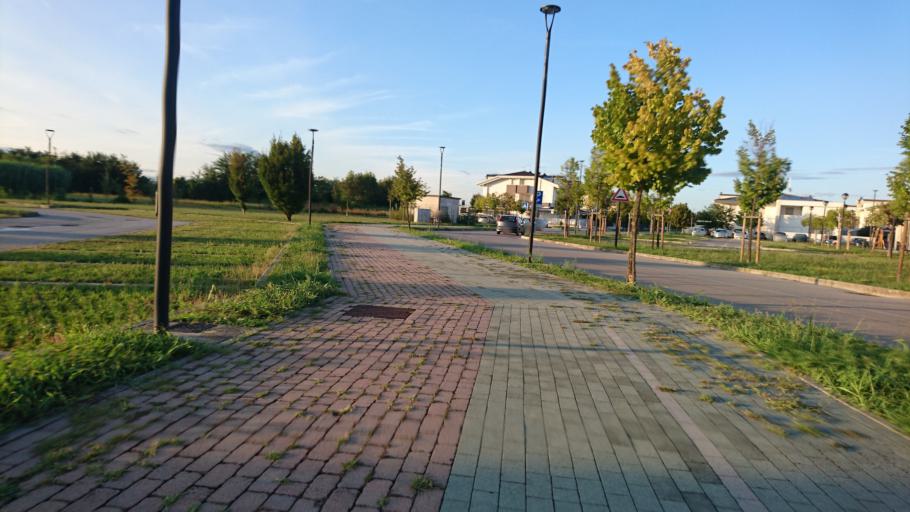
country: IT
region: Veneto
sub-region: Provincia di Padova
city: Montegrotto Terme
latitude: 45.3428
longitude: 11.7910
